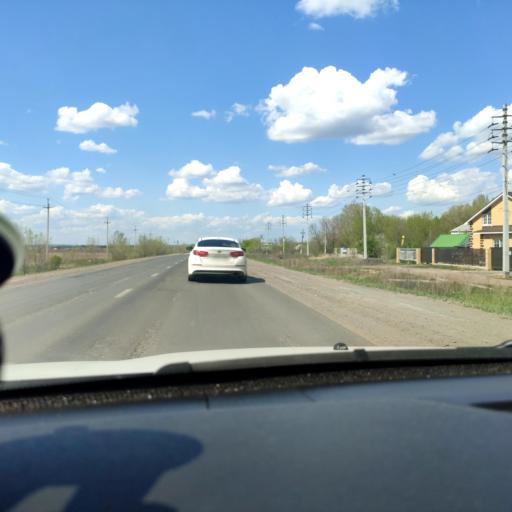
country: RU
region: Samara
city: Kinel'
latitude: 53.2183
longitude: 50.6081
